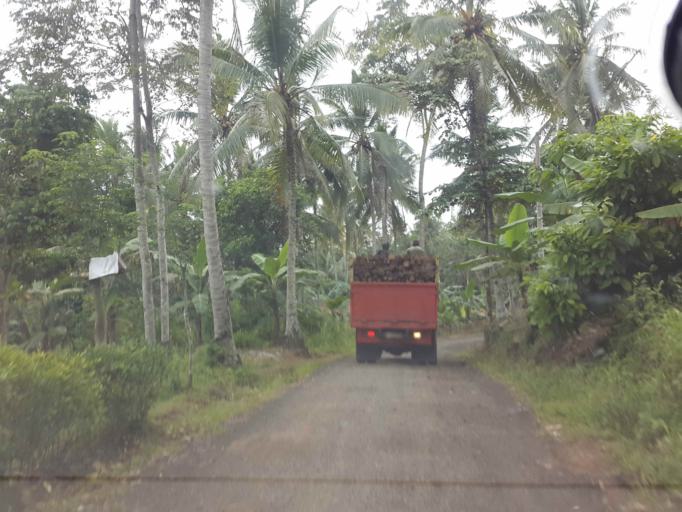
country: ID
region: Lampung
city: Sidorejo
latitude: -5.5665
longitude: 105.4437
